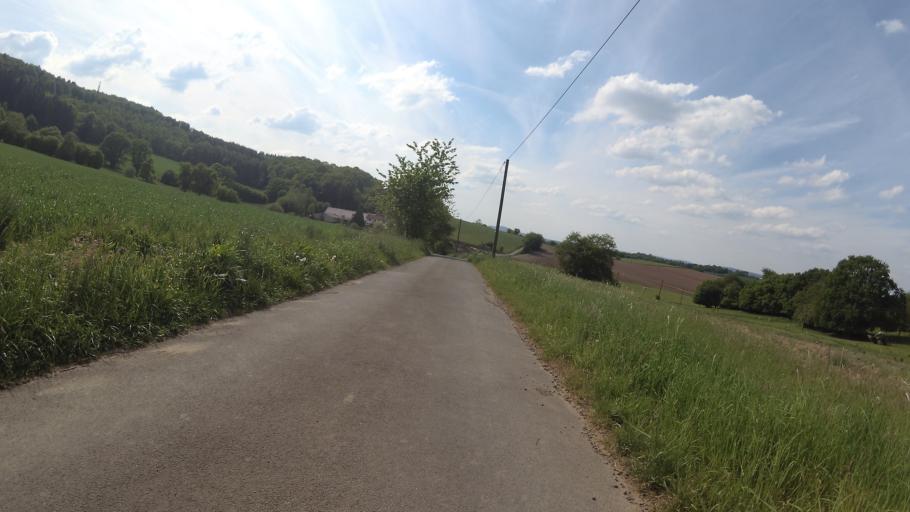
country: DE
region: Saarland
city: Sankt Wendel
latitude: 49.4441
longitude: 7.1751
